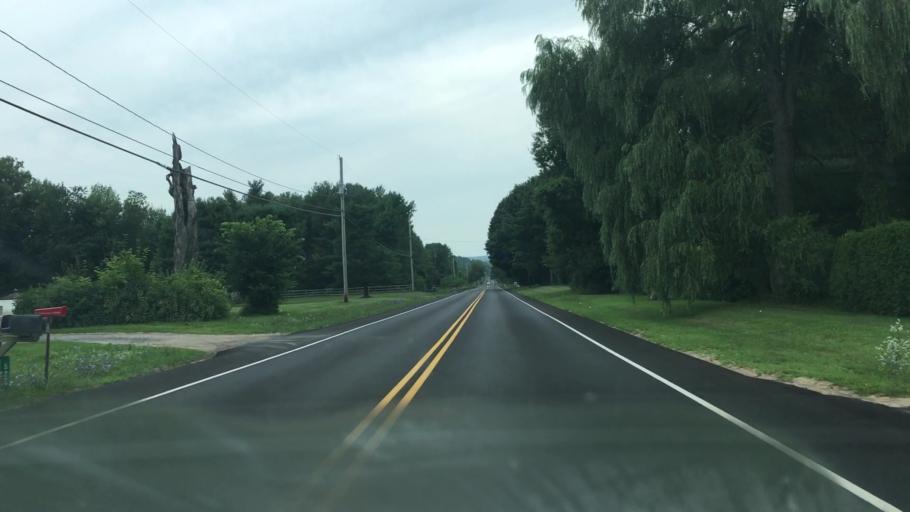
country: US
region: New York
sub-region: Clinton County
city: Plattsburgh West
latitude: 44.6514
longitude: -73.5296
